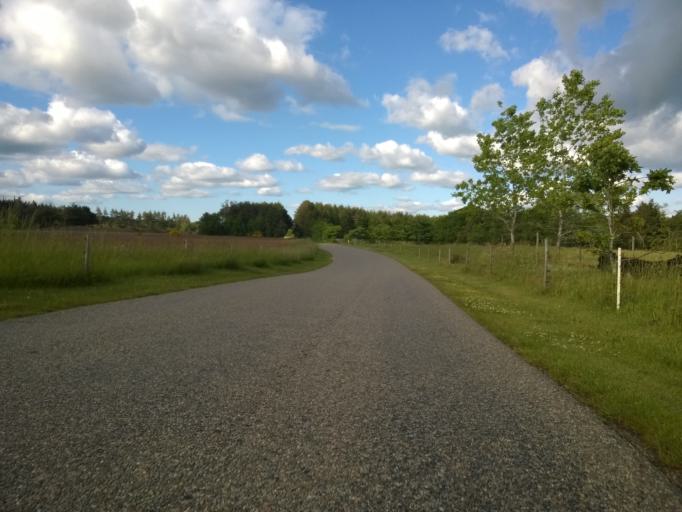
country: DK
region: Central Jutland
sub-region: Holstebro Kommune
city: Vinderup
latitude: 56.4991
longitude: 8.8380
